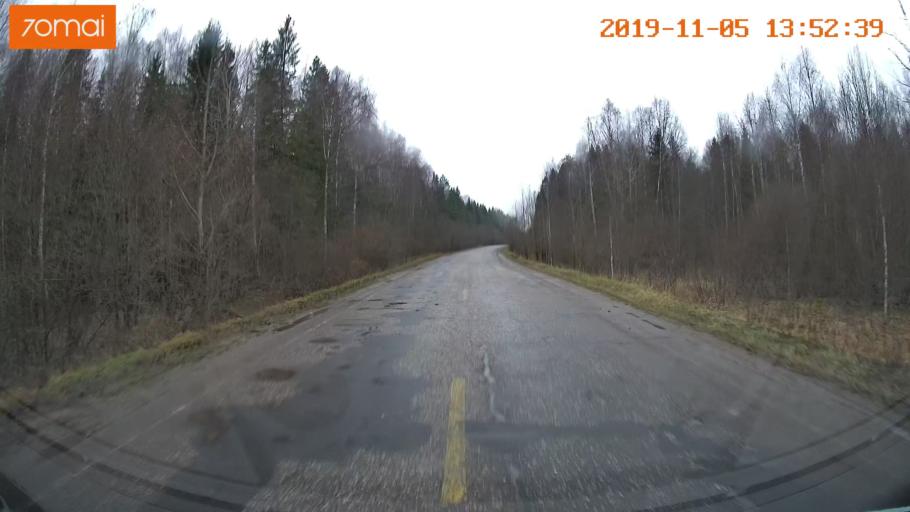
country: RU
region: Ivanovo
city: Kaminskiy
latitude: 57.0284
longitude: 41.3828
